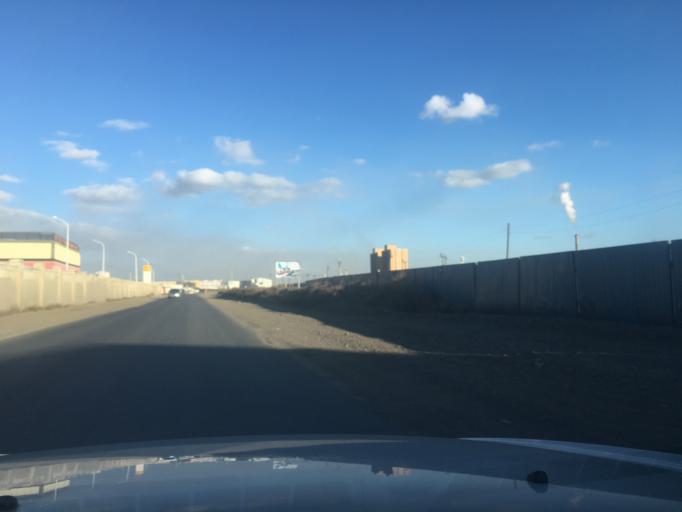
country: MN
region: Ulaanbaatar
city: Ulaanbaatar
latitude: 47.9079
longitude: 106.7665
